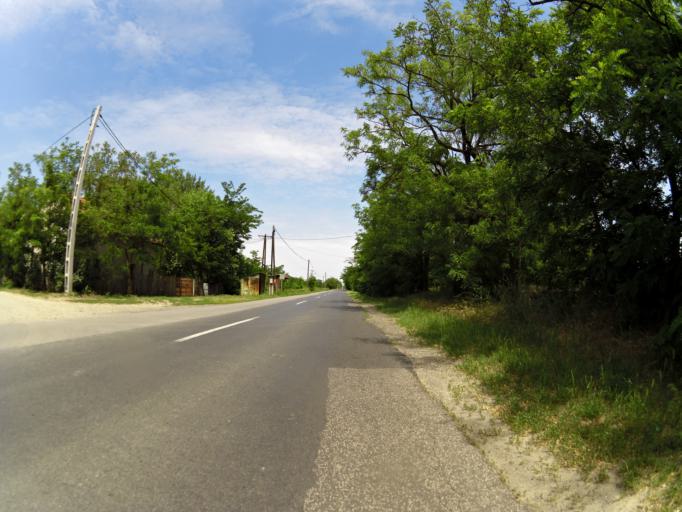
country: HU
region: Csongrad
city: Sandorfalva
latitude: 46.3940
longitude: 20.1143
